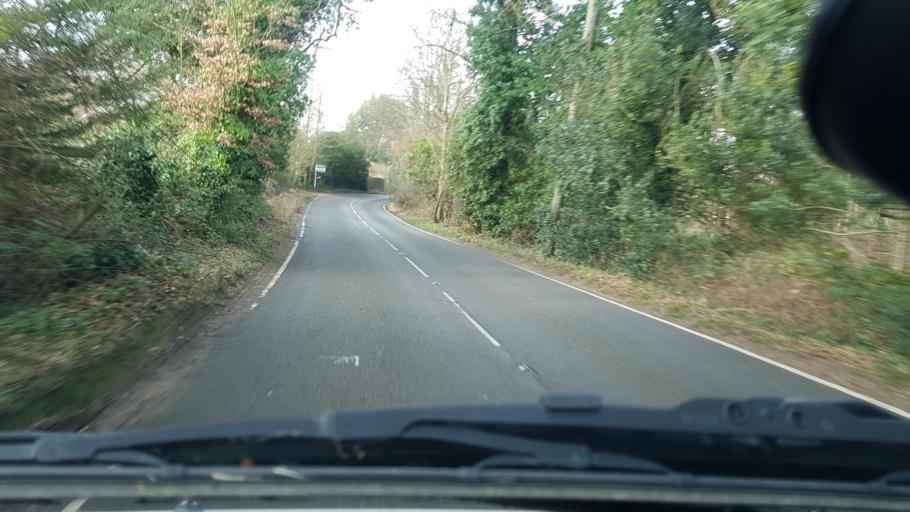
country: GB
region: England
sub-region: Surrey
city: East Horsley
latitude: 51.3096
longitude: -0.4443
